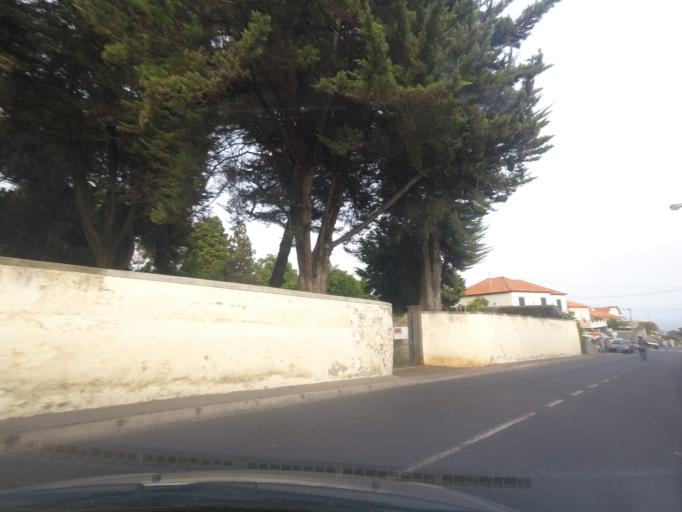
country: PT
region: Madeira
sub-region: Funchal
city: Nossa Senhora do Monte
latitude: 32.6601
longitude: -16.9226
